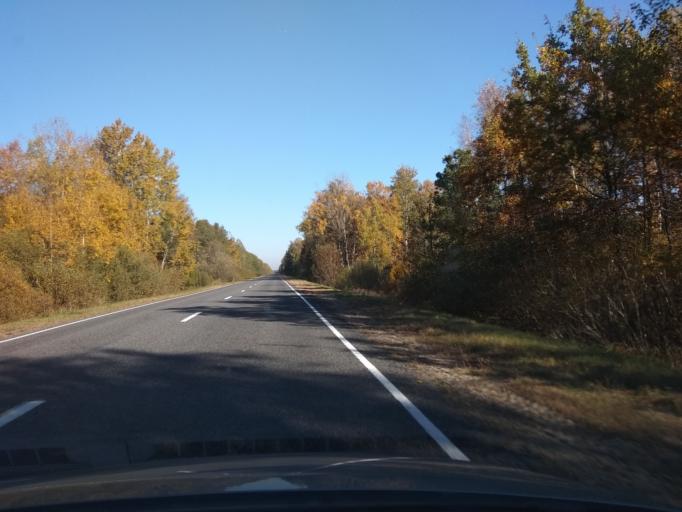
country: BY
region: Brest
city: Malaryta
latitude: 51.9382
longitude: 24.1738
